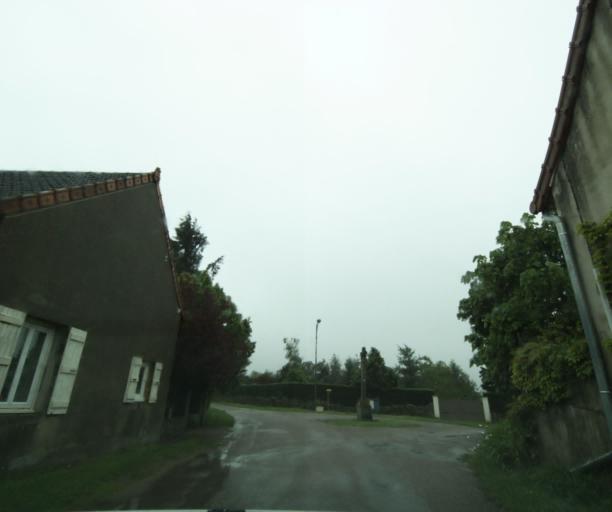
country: FR
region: Bourgogne
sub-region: Departement de Saone-et-Loire
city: Charolles
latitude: 46.3886
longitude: 4.3124
